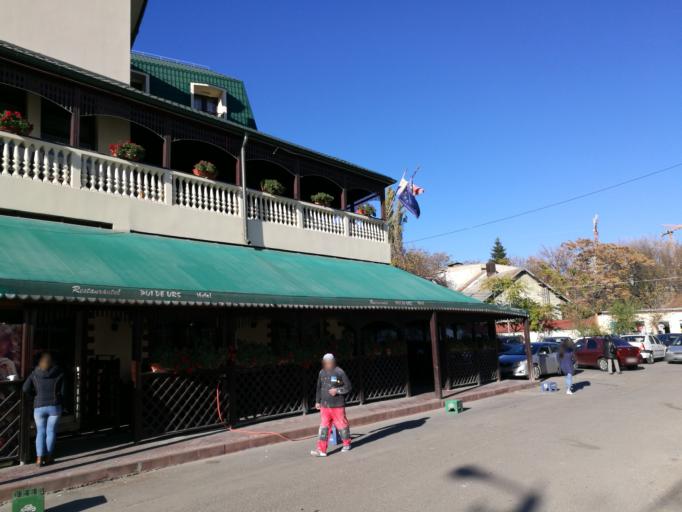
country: RO
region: Bucuresti
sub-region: Municipiul Bucuresti
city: Bucuresti
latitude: 44.4408
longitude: 26.0556
